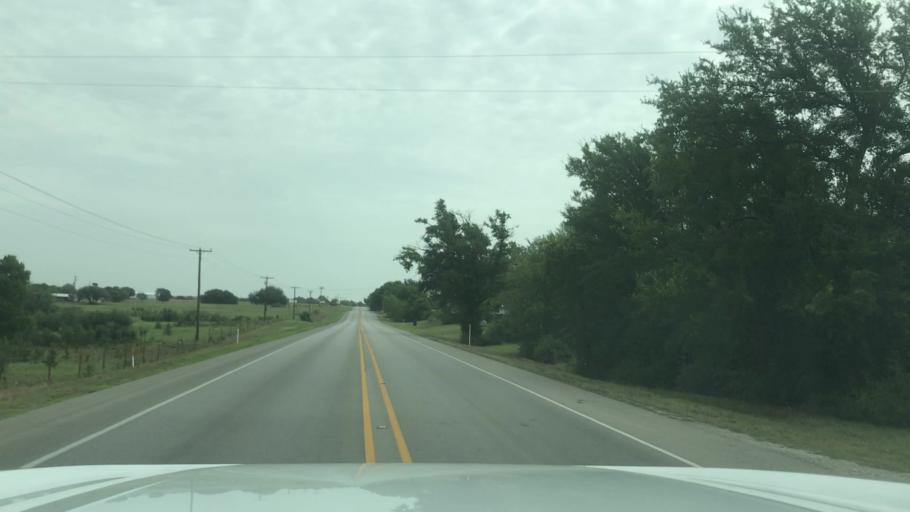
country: US
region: Texas
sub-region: Erath County
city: Dublin
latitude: 32.0912
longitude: -98.4203
